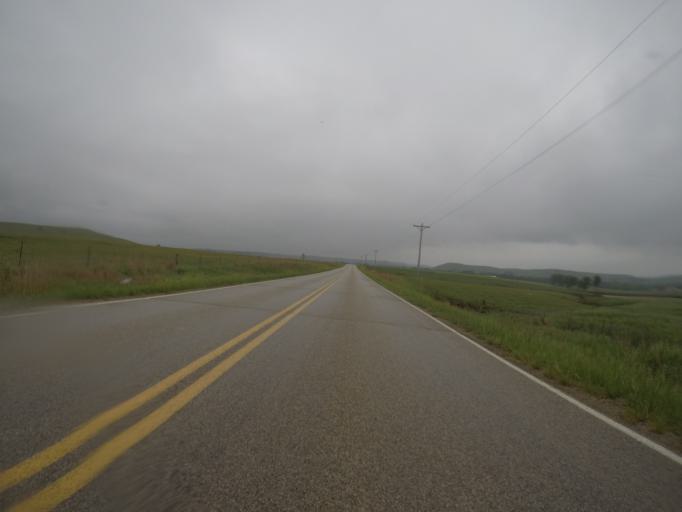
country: US
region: Kansas
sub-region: Pottawatomie County
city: Westmoreland
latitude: 39.4113
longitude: -96.1839
